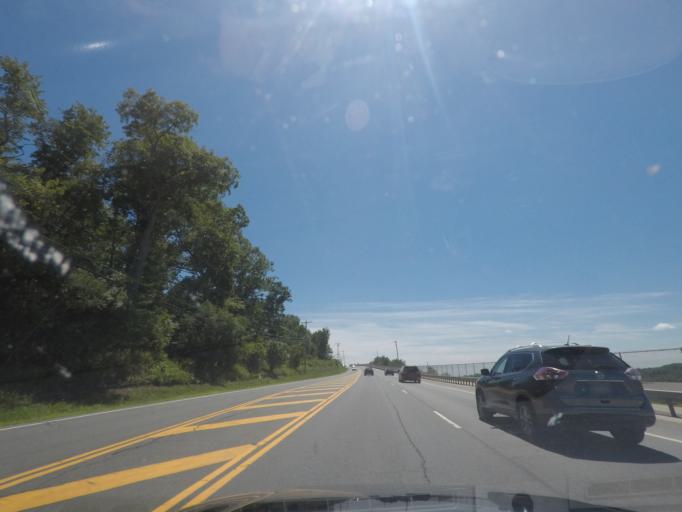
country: US
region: New York
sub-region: Rensselaer County
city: Hampton Manor
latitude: 42.6377
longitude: -73.7004
